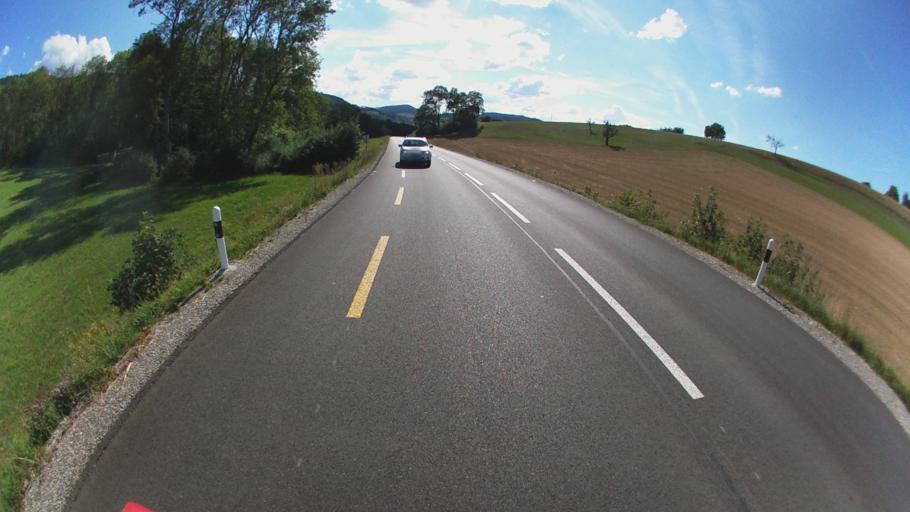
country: CH
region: Aargau
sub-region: Bezirk Rheinfelden
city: Wegenstetten
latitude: 47.5062
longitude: 7.9533
